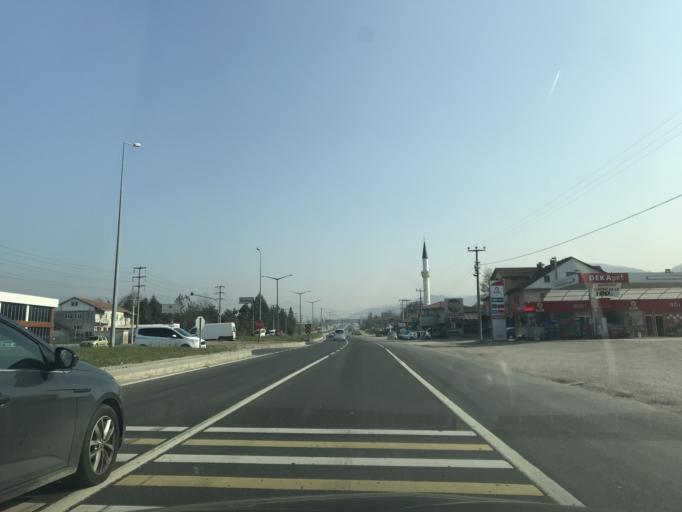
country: TR
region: Duzce
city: Kaynasli
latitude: 40.7786
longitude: 31.2887
